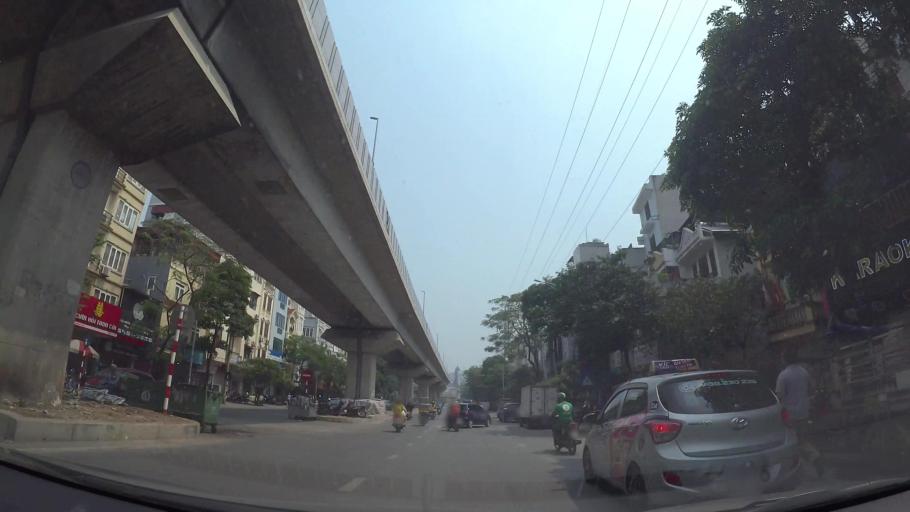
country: VN
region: Ha Noi
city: Dong Da
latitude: 21.0240
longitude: 105.8269
